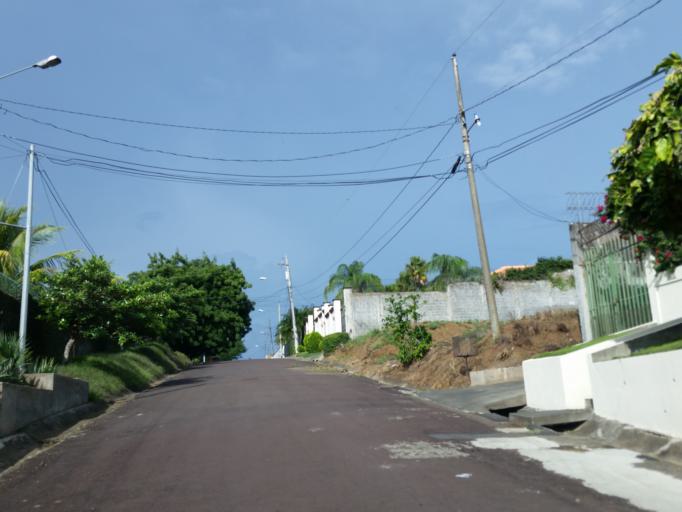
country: NI
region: Managua
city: El Crucero
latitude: 12.0732
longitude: -86.3230
